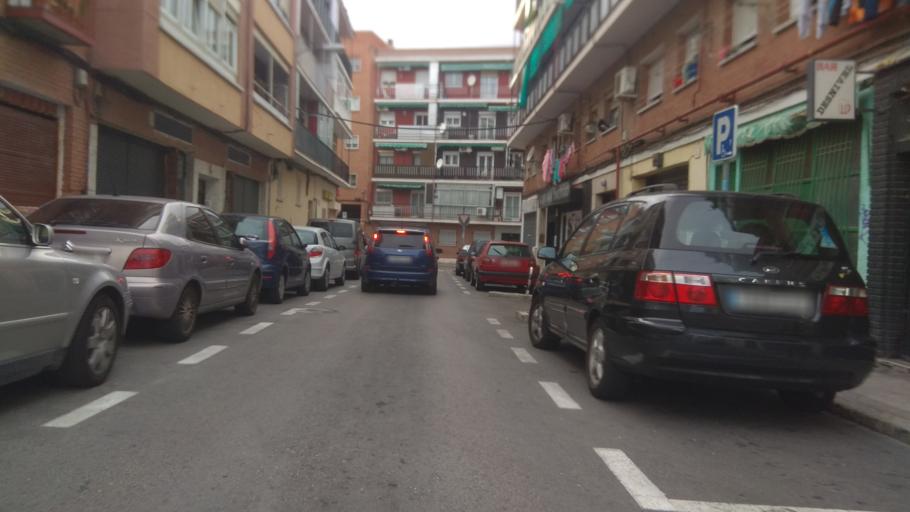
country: ES
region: Madrid
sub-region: Provincia de Madrid
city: Vicalvaro
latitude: 40.4058
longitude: -3.6040
